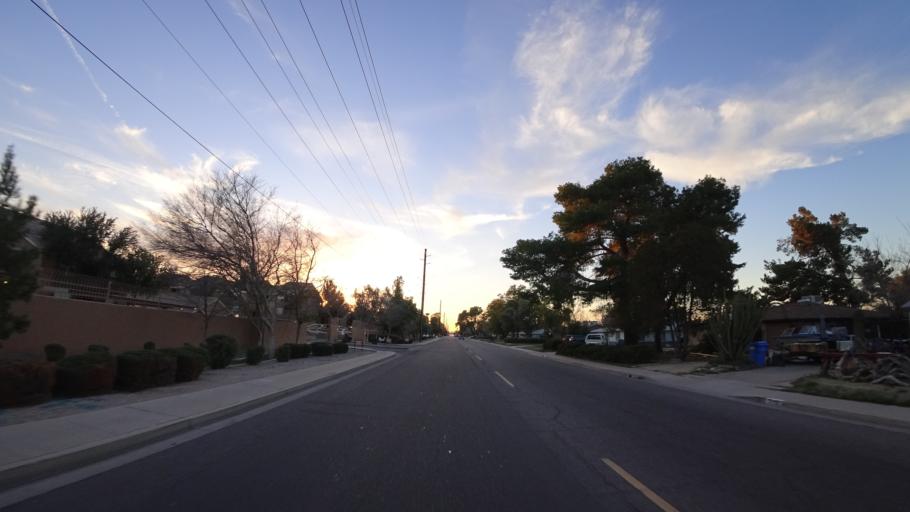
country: US
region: Arizona
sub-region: Maricopa County
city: Tempe Junction
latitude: 33.4729
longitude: -111.9896
